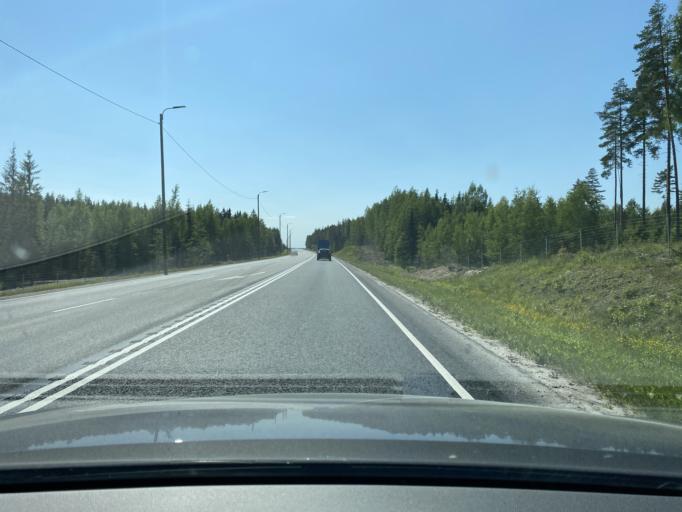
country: FI
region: Pirkanmaa
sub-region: Lounais-Pirkanmaa
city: Mouhijaervi
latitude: 61.3780
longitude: 23.1544
